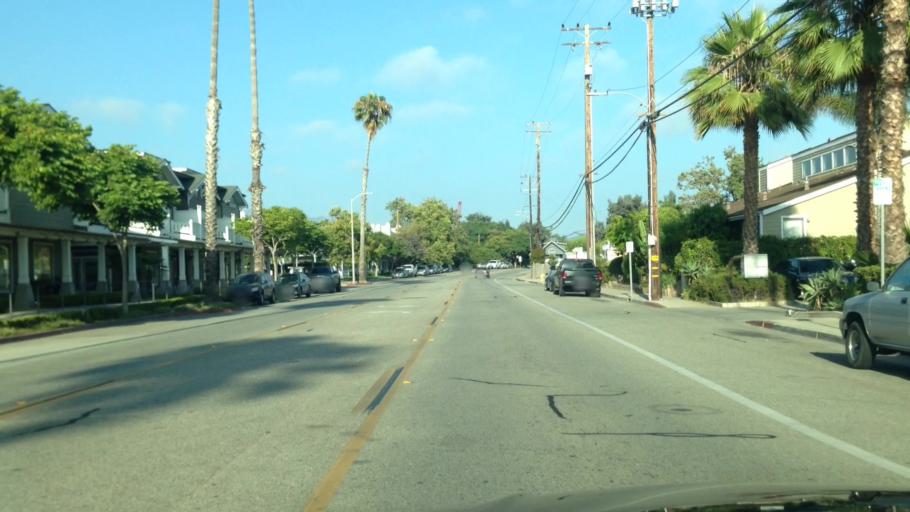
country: US
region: California
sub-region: Santa Barbara County
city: Carpinteria
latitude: 34.4016
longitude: -119.5239
